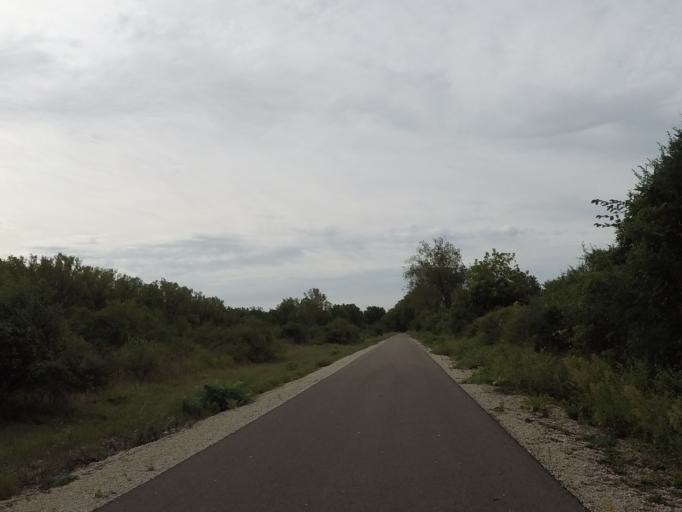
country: US
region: Wisconsin
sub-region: Sauk County
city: Prairie du Sac
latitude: 43.3500
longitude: -89.7407
